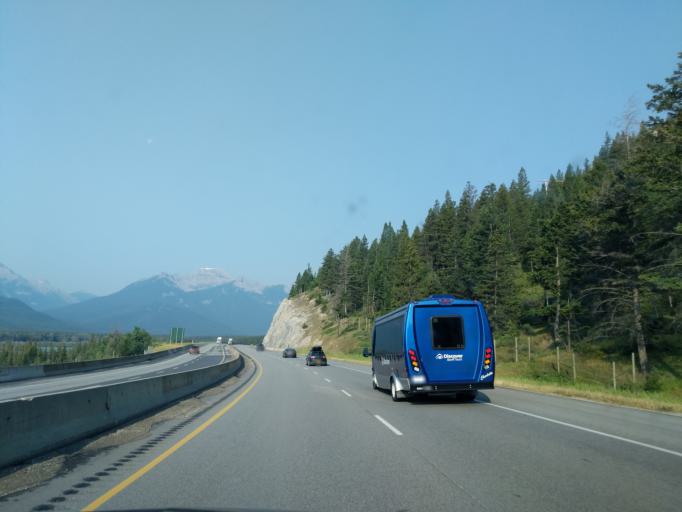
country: CA
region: Alberta
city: Banff
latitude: 51.1795
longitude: -115.6192
